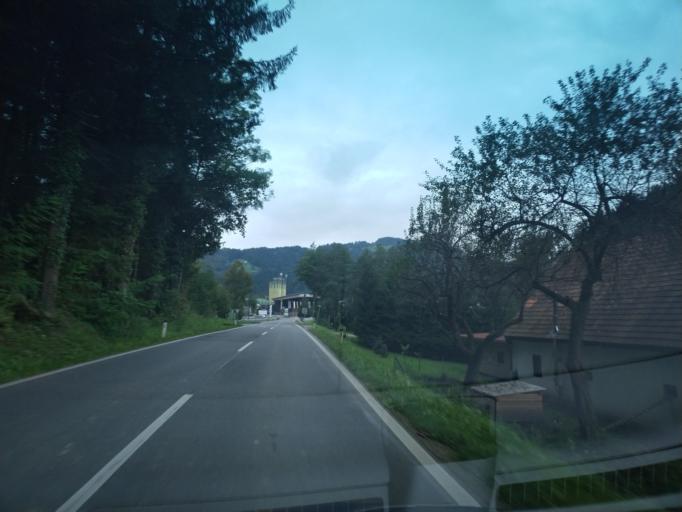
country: AT
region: Styria
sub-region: Politischer Bezirk Deutschlandsberg
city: Wernersdorf
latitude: 46.7168
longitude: 15.2172
